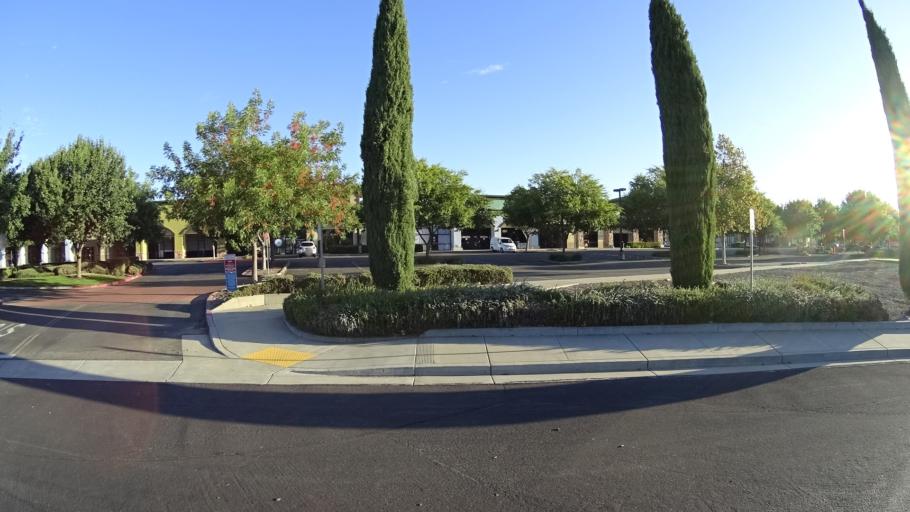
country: US
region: California
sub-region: Sacramento County
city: Laguna
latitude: 38.4077
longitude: -121.4803
